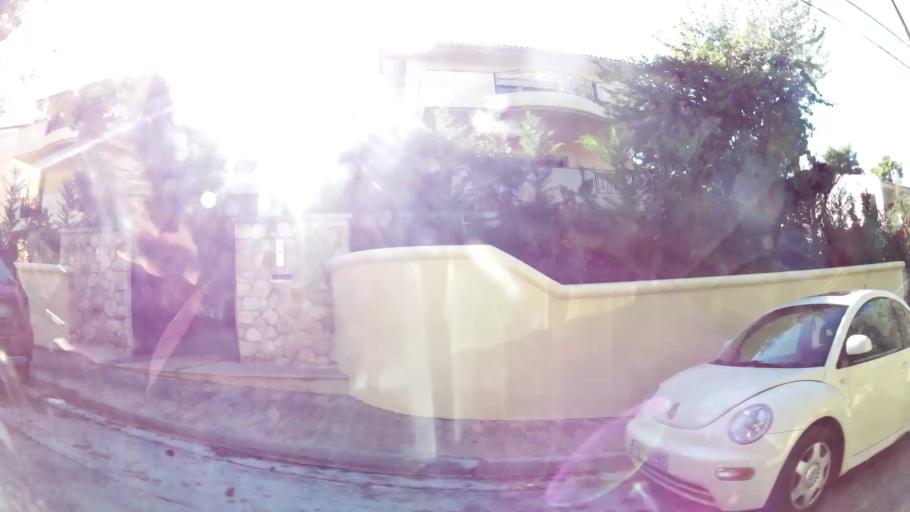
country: GR
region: Attica
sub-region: Nomarchia Anatolikis Attikis
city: Drosia
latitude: 38.1154
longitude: 23.8645
